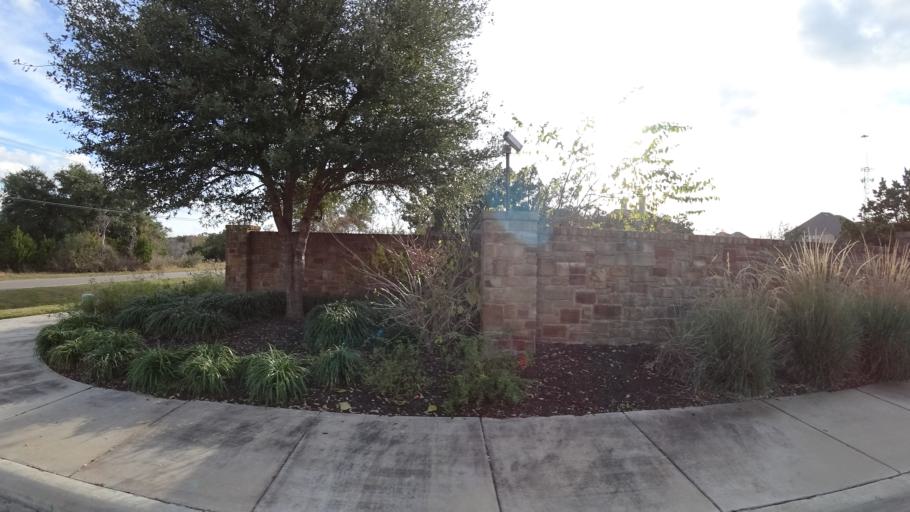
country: US
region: Texas
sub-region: Williamson County
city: Brushy Creek
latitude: 30.5054
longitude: -97.7197
